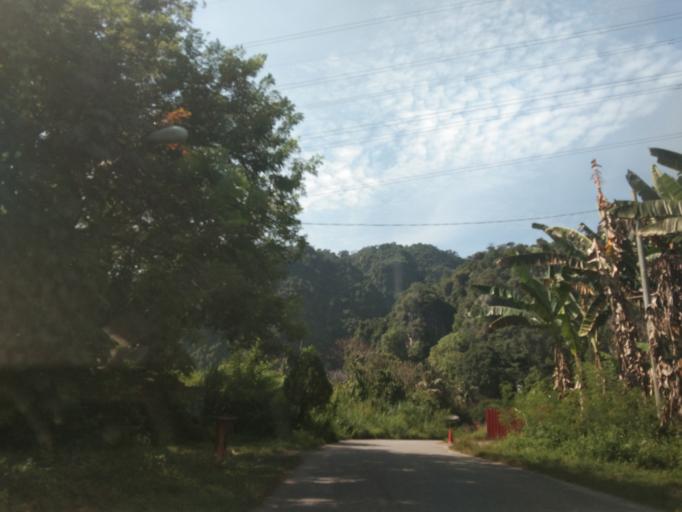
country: MY
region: Perak
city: Ipoh
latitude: 4.5643
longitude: 101.1298
